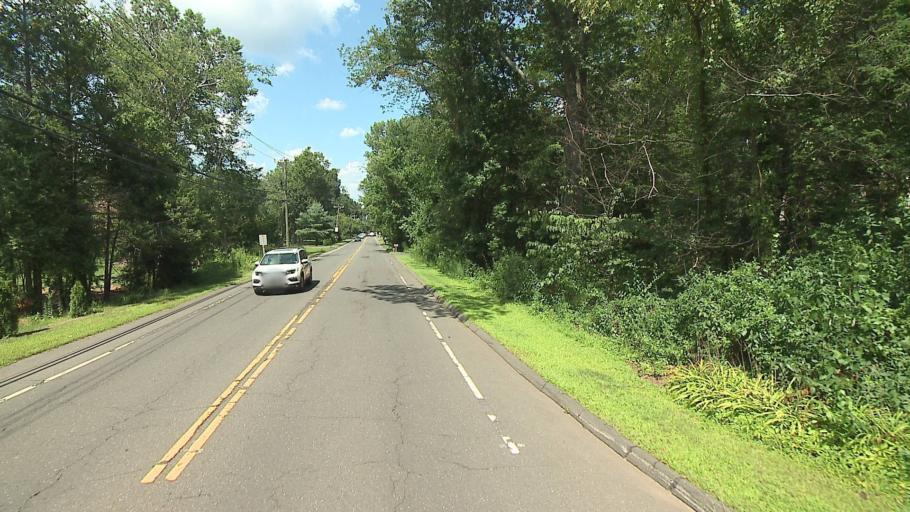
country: US
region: Connecticut
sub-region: Hartford County
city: Farmington
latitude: 41.7170
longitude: -72.8070
